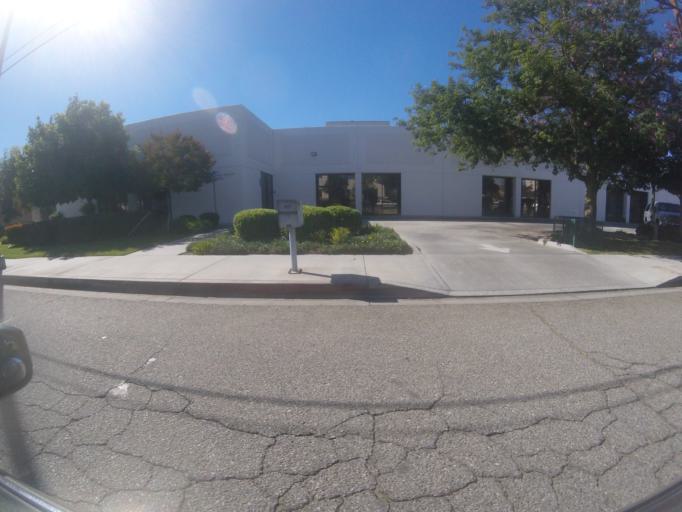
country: US
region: California
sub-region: San Bernardino County
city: Redlands
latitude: 34.0610
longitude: -117.2218
